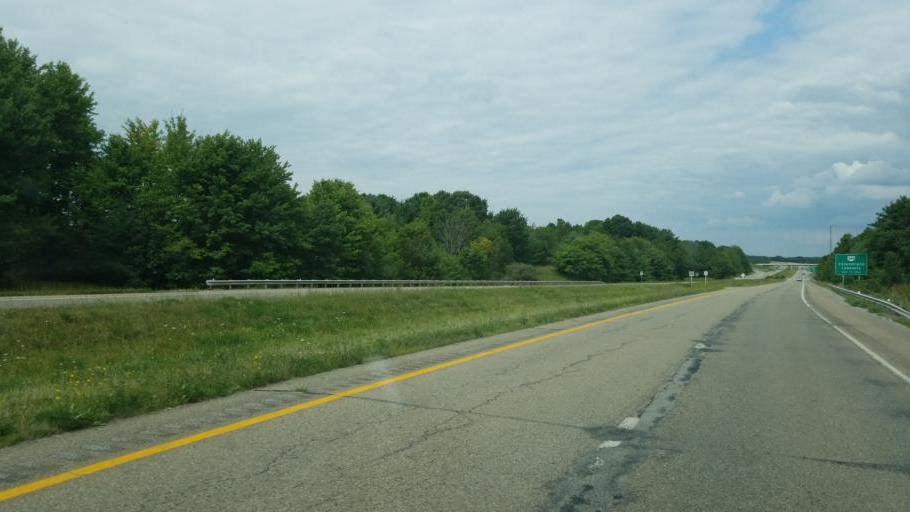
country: US
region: Ohio
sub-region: Columbiana County
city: Leetonia
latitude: 40.8709
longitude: -80.7317
